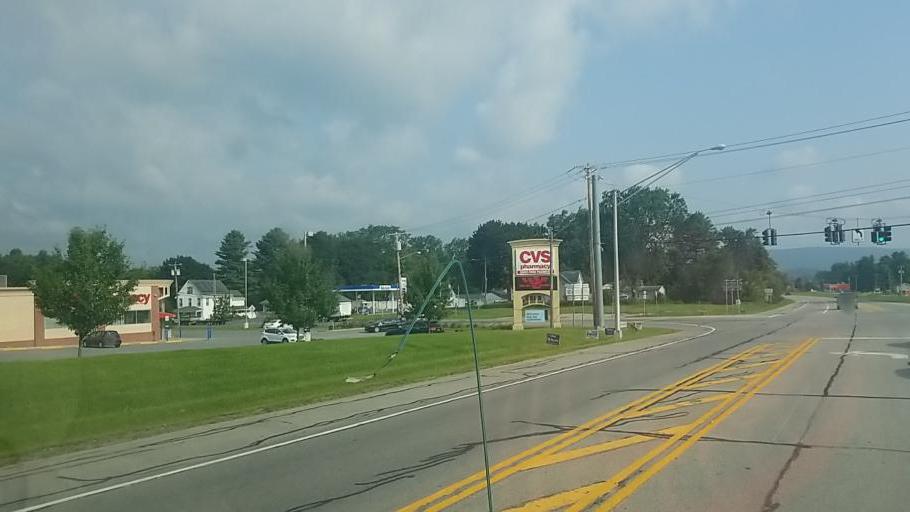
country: US
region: New York
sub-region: Fulton County
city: Gloversville
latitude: 43.0506
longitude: -74.3223
